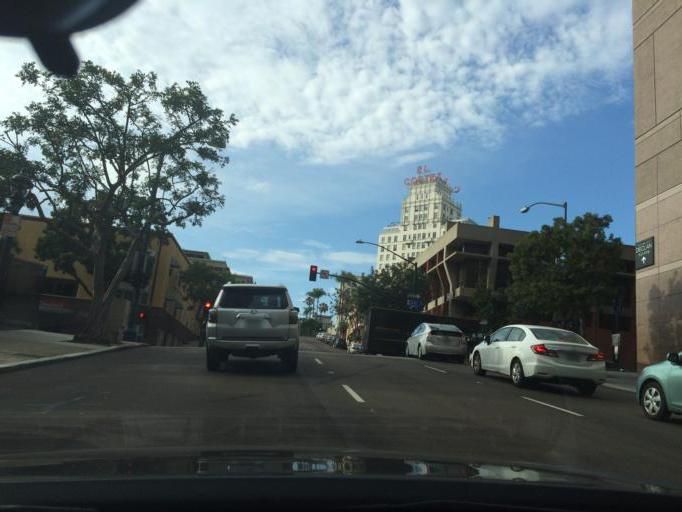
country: US
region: California
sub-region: San Diego County
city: San Diego
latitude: 32.7185
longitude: -117.1583
